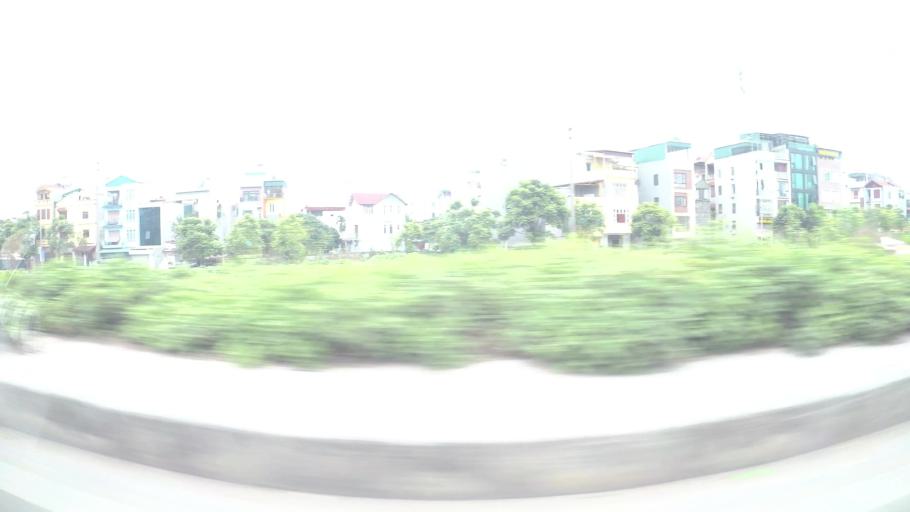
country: VN
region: Ha Noi
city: Hoan Kiem
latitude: 21.0710
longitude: 105.8821
